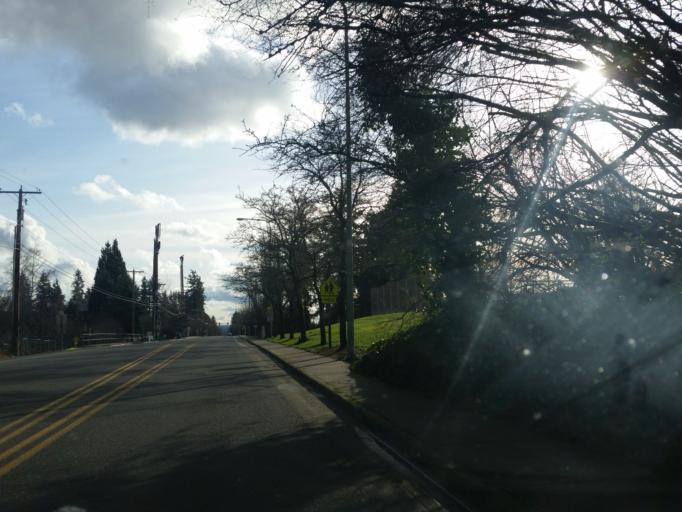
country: US
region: Washington
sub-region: King County
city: Kingsgate
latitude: 47.7295
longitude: -122.1640
